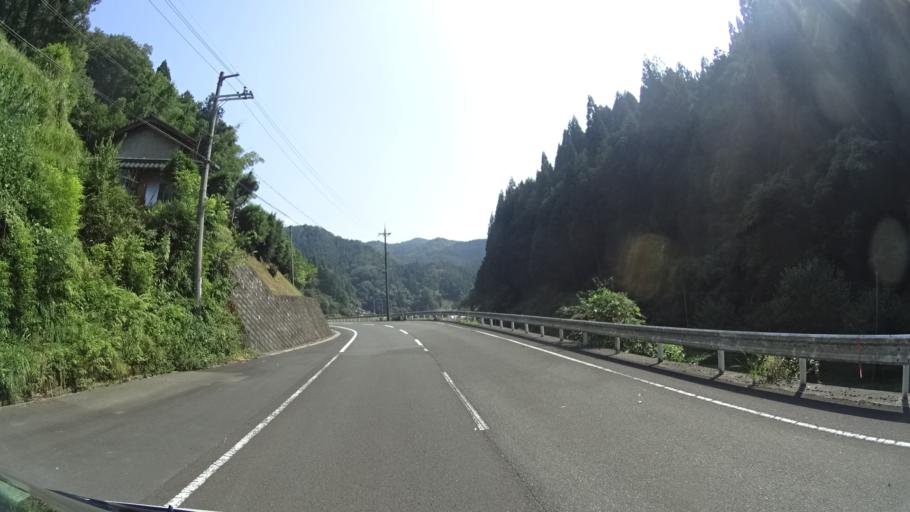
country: JP
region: Kyoto
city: Maizuru
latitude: 35.4133
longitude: 135.2311
